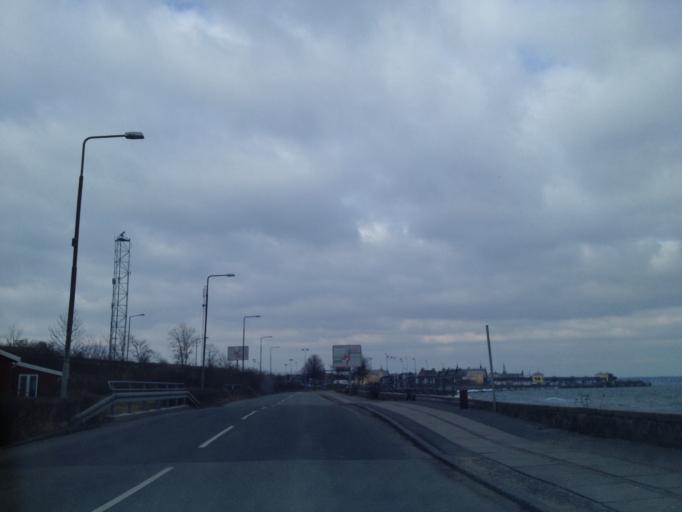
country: DK
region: Capital Region
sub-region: Helsingor Kommune
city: Helsingor
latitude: 56.0267
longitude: 12.6072
